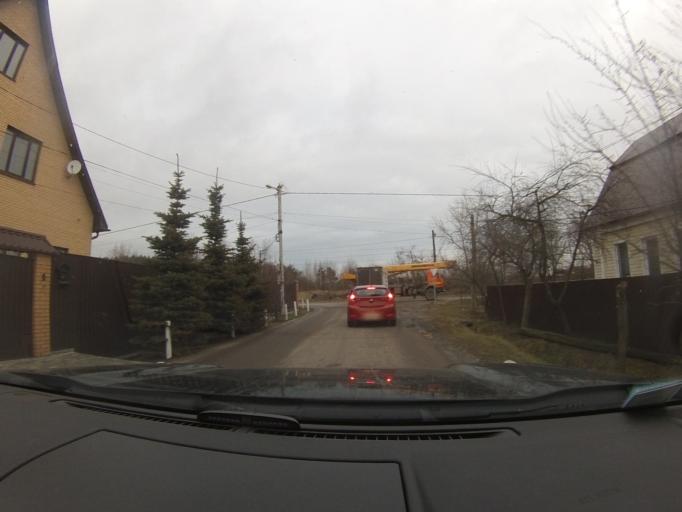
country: RU
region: Moskovskaya
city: Voskresensk
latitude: 55.3292
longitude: 38.6796
